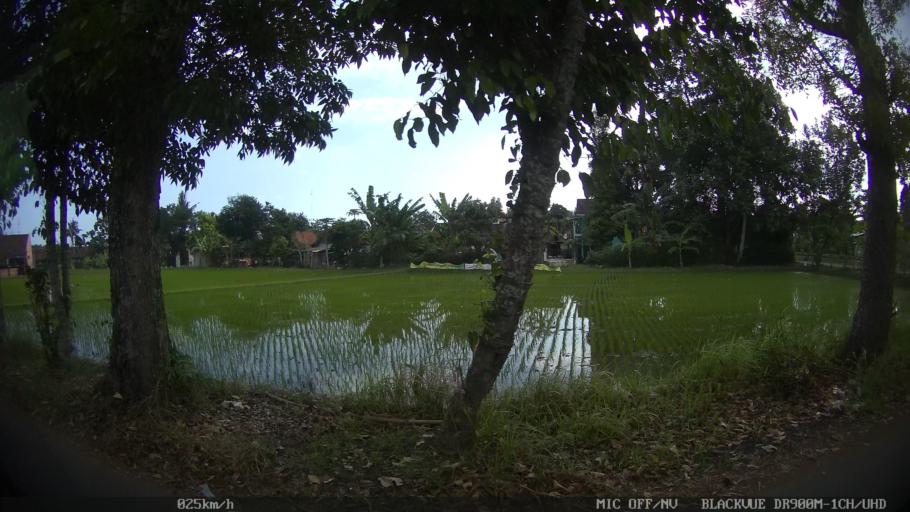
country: ID
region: Daerah Istimewa Yogyakarta
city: Gamping Lor
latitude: -7.7891
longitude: 110.3363
